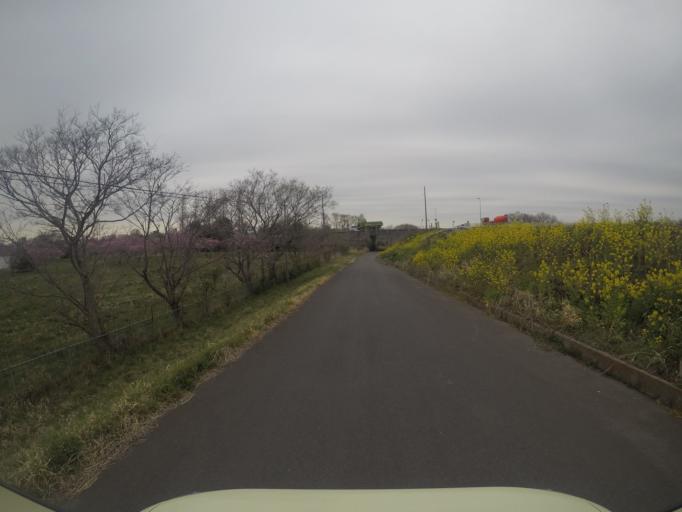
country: JP
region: Ibaraki
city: Ishige
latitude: 36.0770
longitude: 140.0040
